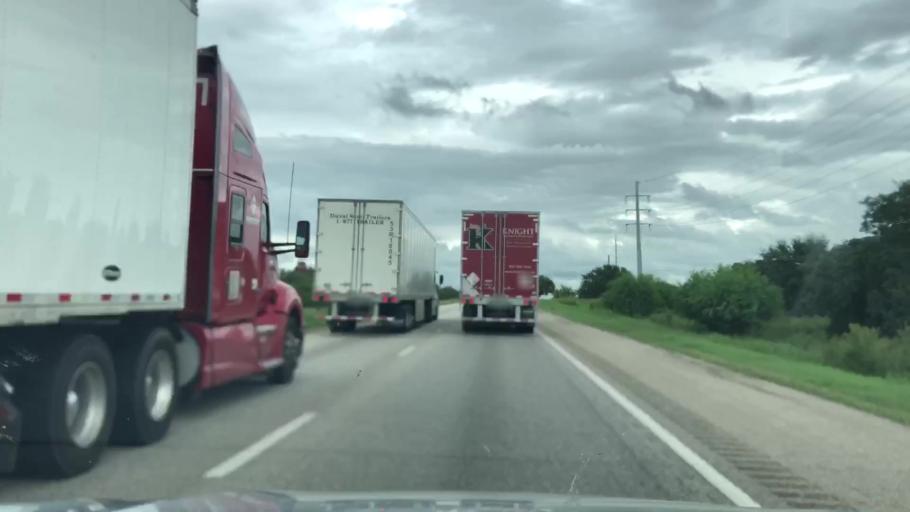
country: US
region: Texas
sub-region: Guadalupe County
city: Seguin
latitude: 29.5991
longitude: -97.9332
